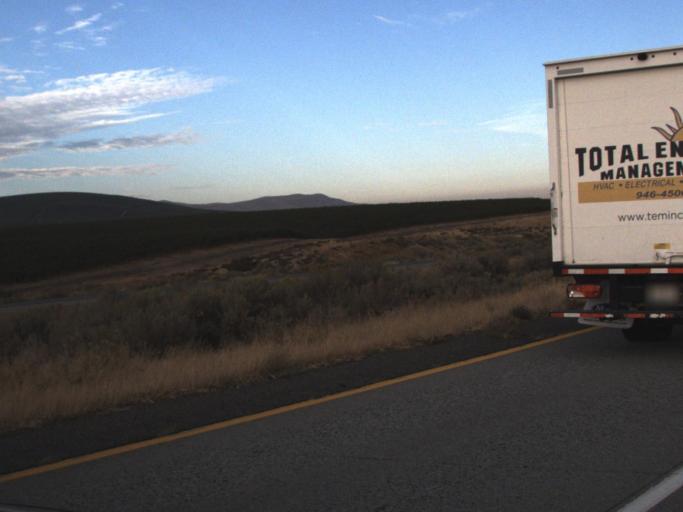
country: US
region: Washington
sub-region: Benton County
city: West Richland
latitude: 46.2566
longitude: -119.3819
